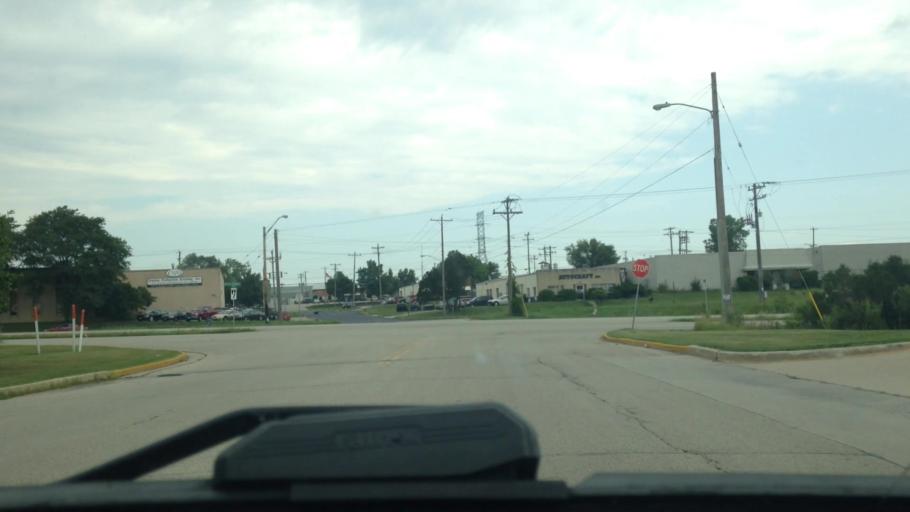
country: US
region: Wisconsin
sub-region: Waukesha County
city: Butler
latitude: 43.1183
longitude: -88.0790
